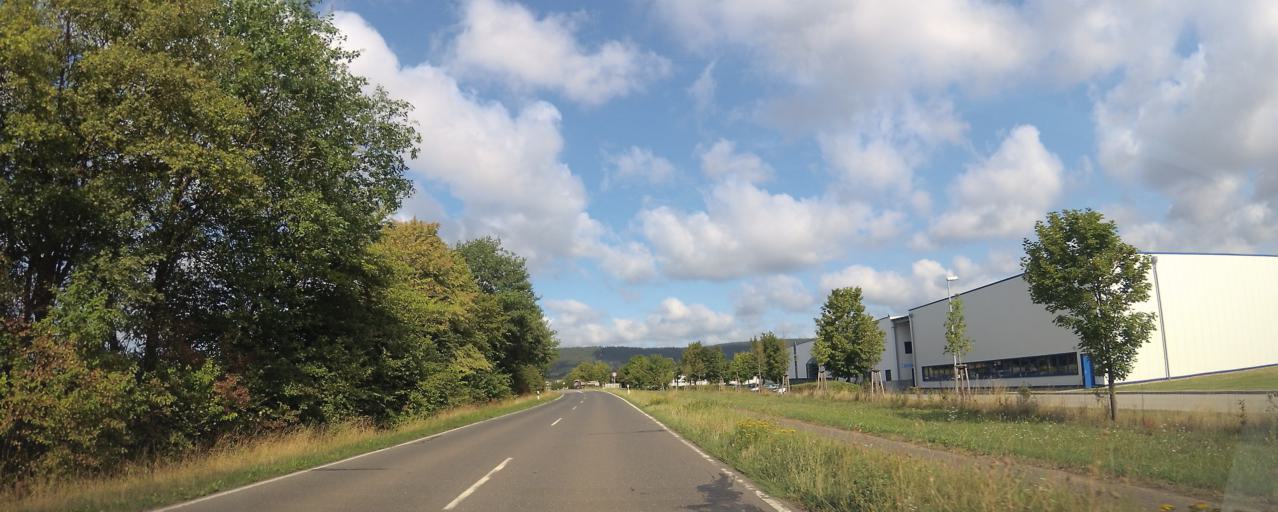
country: DE
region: Rheinland-Pfalz
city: Bekond
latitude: 49.8554
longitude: 6.7844
